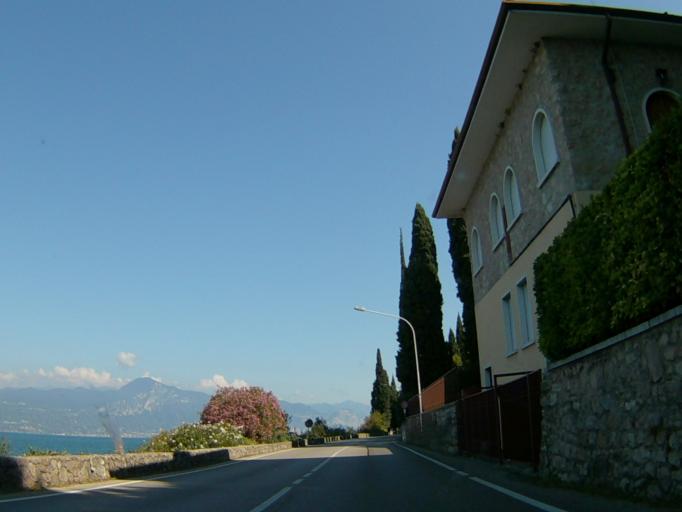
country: IT
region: Veneto
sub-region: Provincia di Verona
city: Torri del Benaco
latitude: 45.5871
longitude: 10.6753
